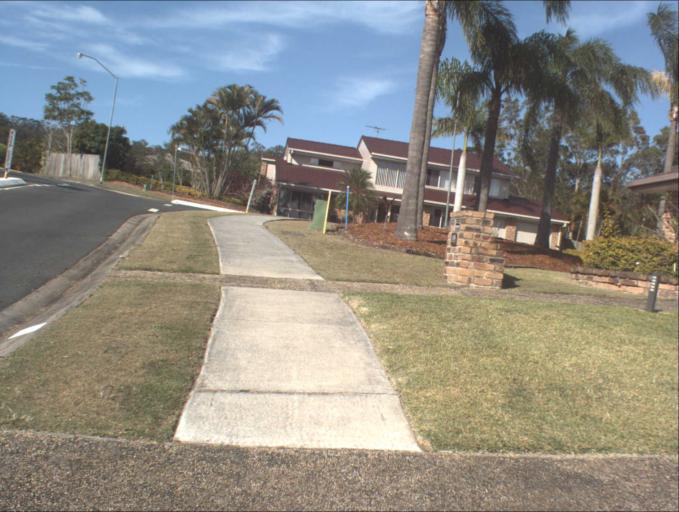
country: AU
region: Queensland
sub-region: Logan
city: Slacks Creek
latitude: -27.6403
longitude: 153.1778
